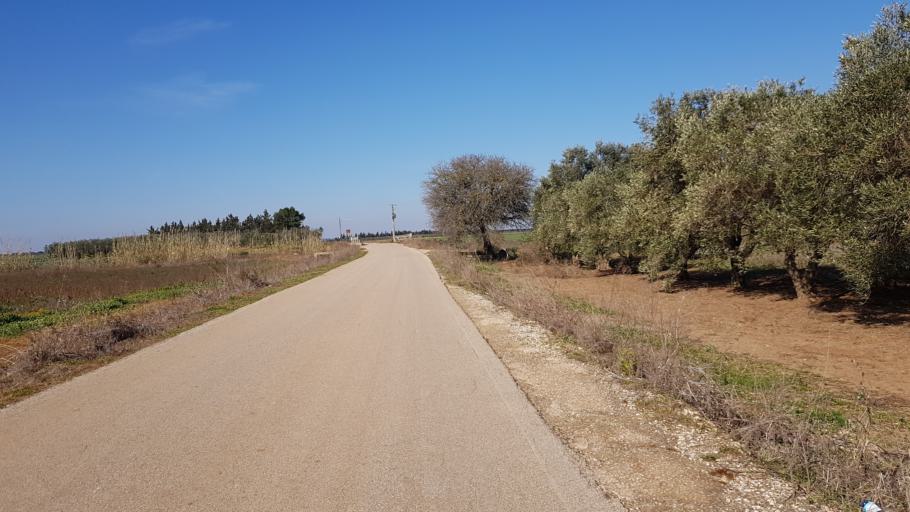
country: IT
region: Apulia
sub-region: Provincia di Brindisi
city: Mesagne
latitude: 40.6192
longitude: 17.8157
